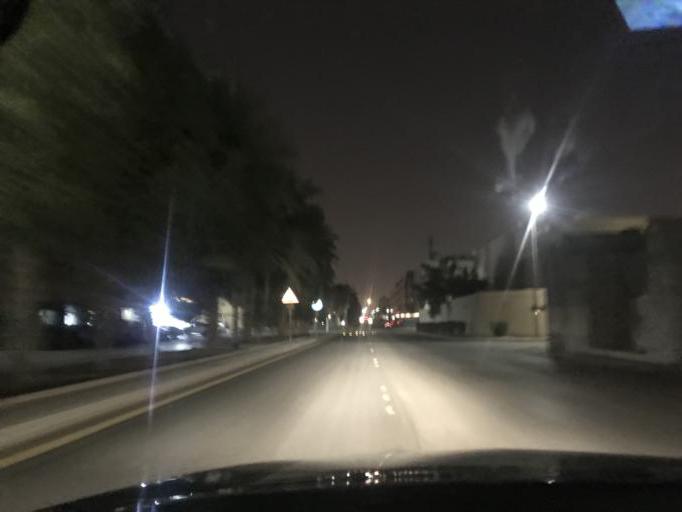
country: SA
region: Ar Riyad
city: Riyadh
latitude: 24.7145
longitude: 46.7769
